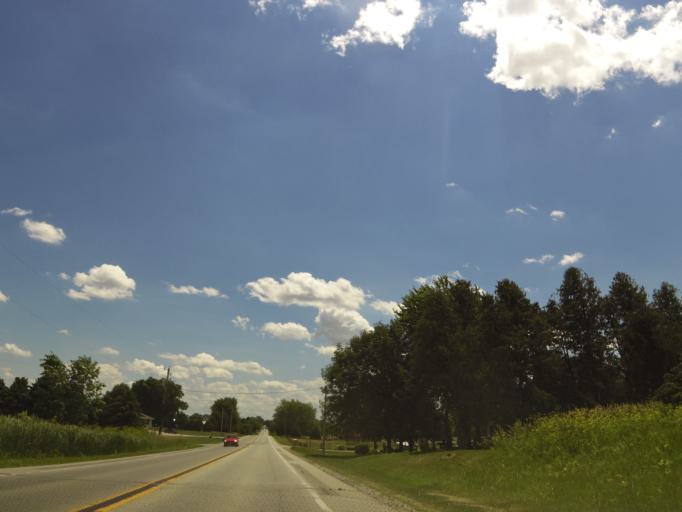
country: US
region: Iowa
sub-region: Buchanan County
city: Independence
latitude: 42.4893
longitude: -91.8895
